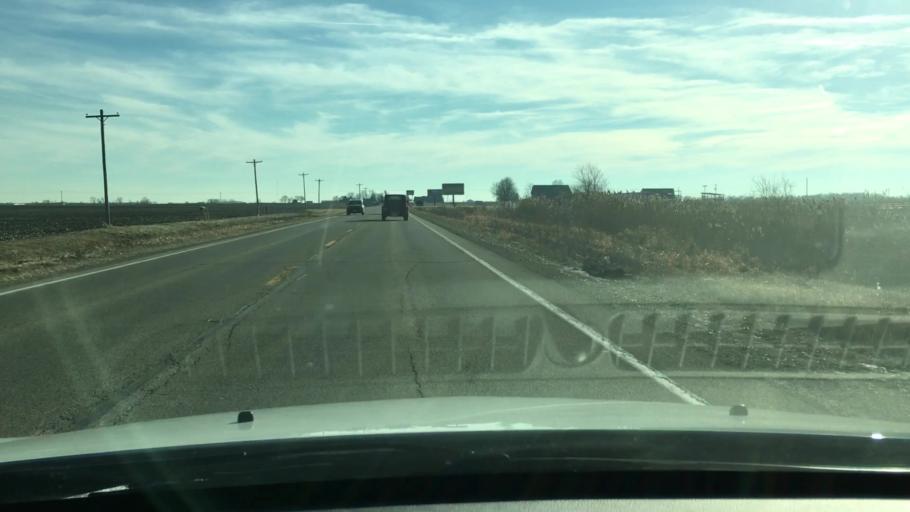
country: US
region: Illinois
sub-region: LaSalle County
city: Mendota
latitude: 41.4887
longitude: -89.1271
